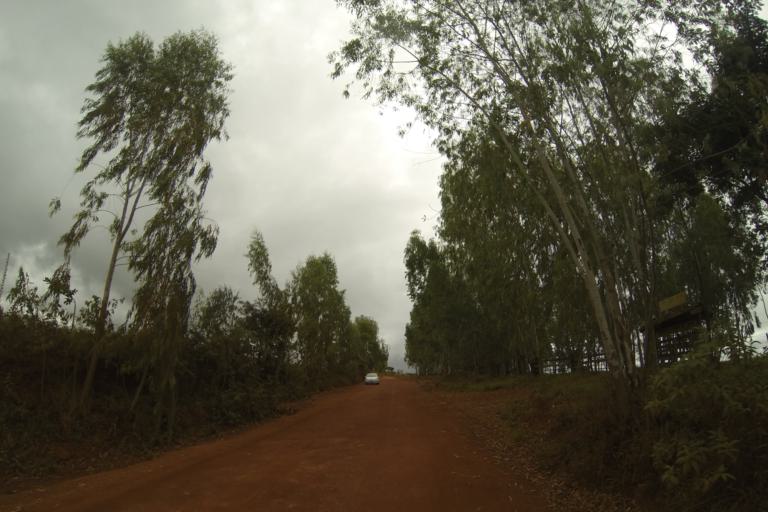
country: BR
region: Minas Gerais
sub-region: Campos Altos
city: Campos Altos
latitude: -19.7819
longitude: -46.3776
